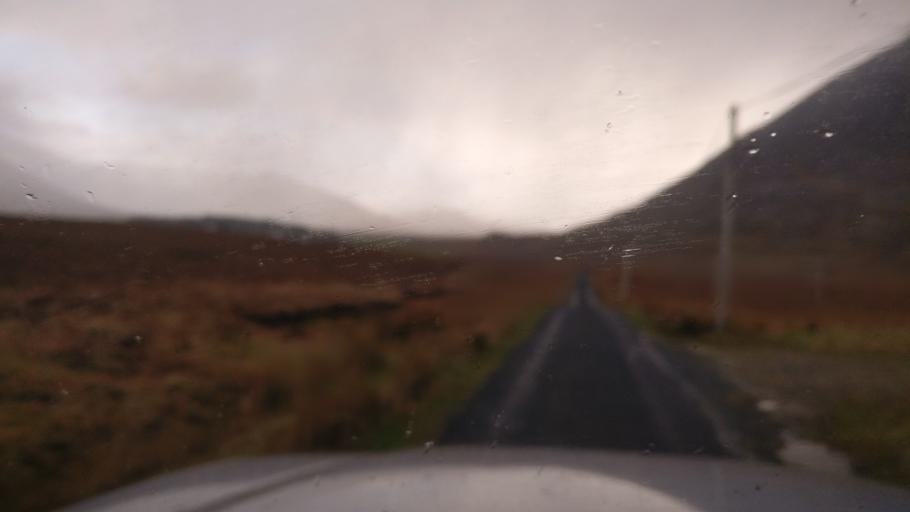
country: IE
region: Connaught
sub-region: County Galway
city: Clifden
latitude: 53.5163
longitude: -9.7177
